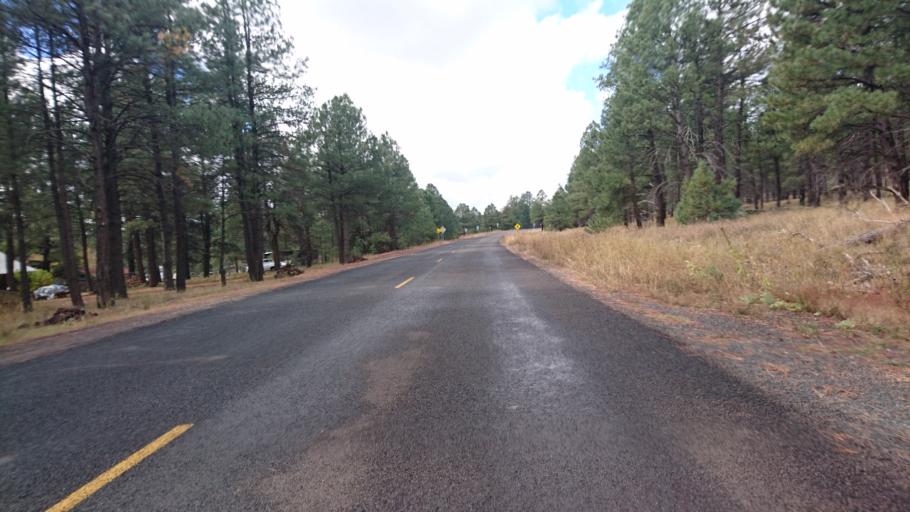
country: US
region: Arizona
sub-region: Coconino County
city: Parks
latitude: 35.2583
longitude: -111.9366
